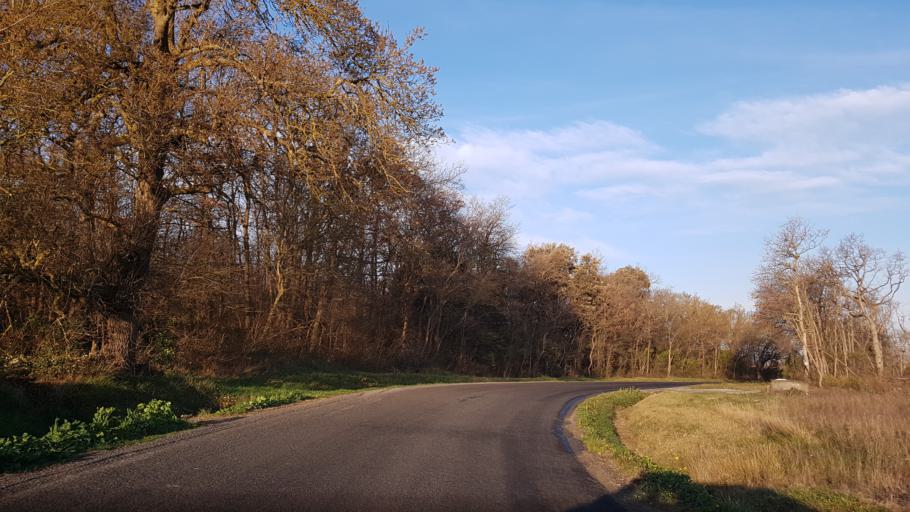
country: FR
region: Languedoc-Roussillon
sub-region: Departement de l'Aude
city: Villeneuve-la-Comptal
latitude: 43.2833
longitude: 1.9349
